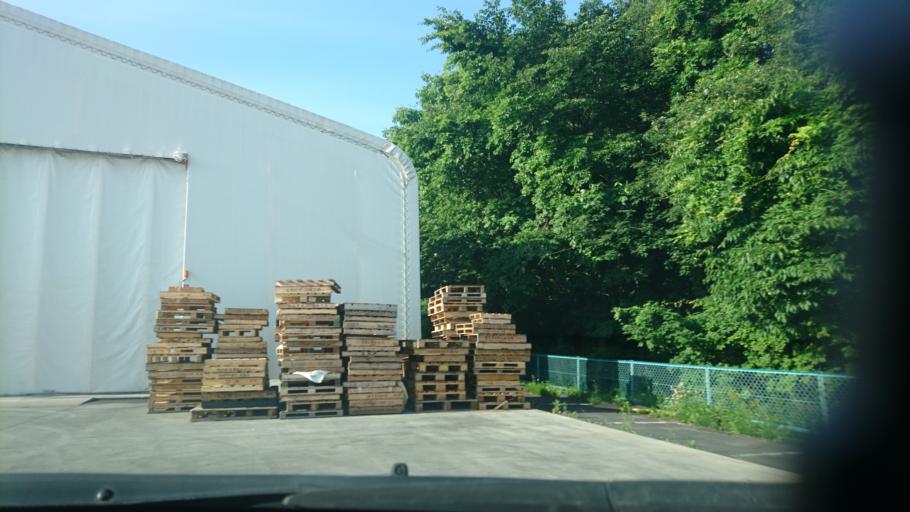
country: JP
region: Iwate
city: Ichinoseki
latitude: 38.9178
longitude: 141.1670
